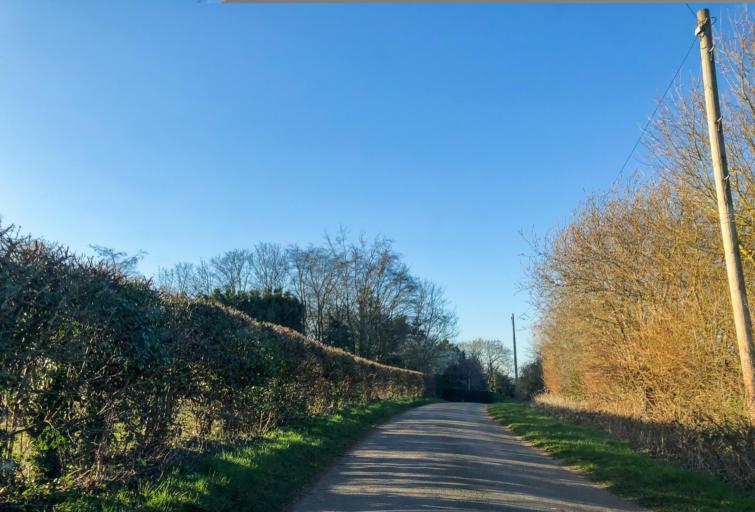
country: GB
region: England
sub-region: Warwickshire
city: Warwick
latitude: 52.2425
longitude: -1.5849
